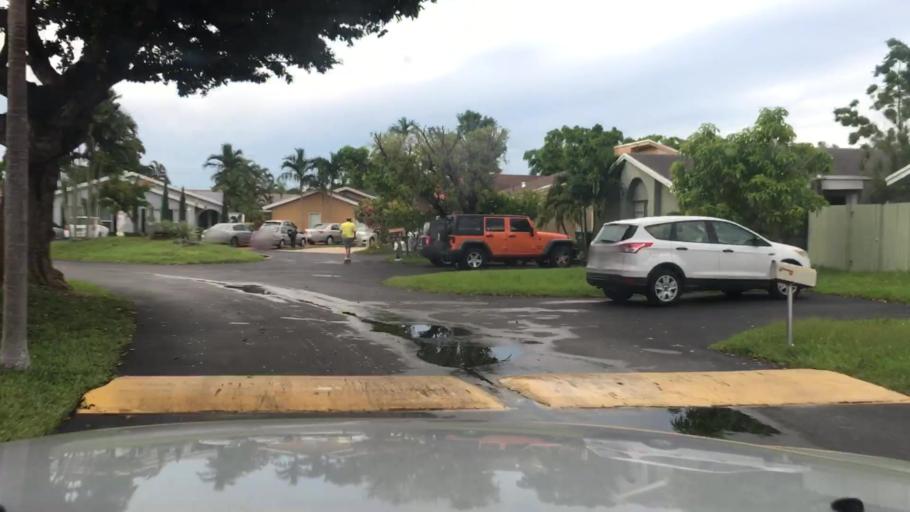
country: US
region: Florida
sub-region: Miami-Dade County
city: Westwood Lake
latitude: 25.7381
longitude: -80.3803
